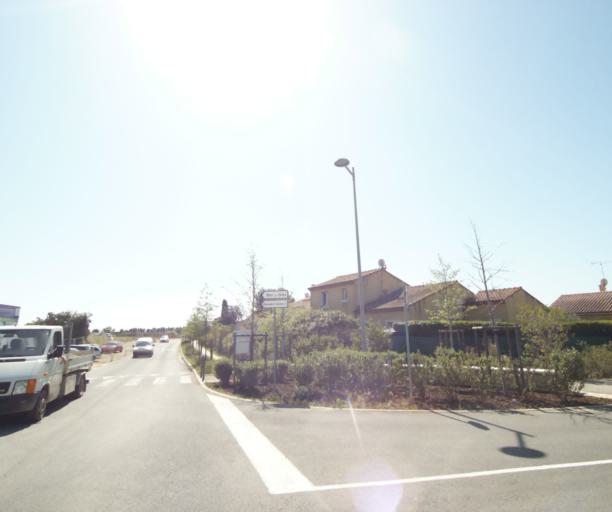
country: FR
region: Languedoc-Roussillon
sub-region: Departement de l'Herault
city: Saint-Bres
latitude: 43.6693
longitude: 4.0365
